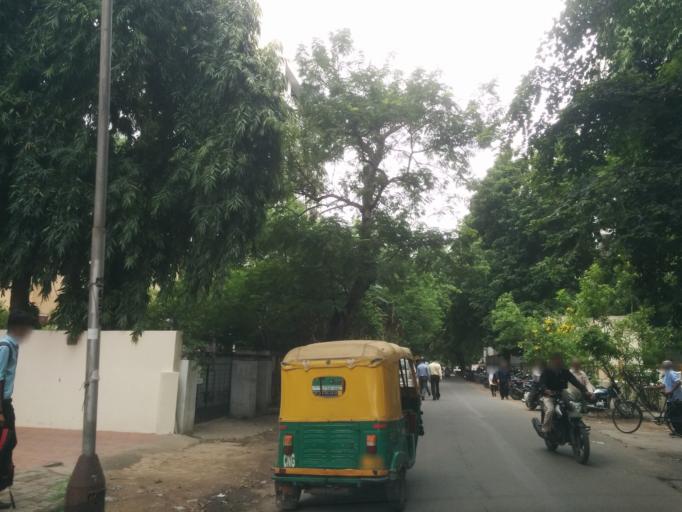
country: IN
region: Gujarat
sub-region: Ahmadabad
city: Ahmedabad
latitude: 23.0304
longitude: 72.5624
